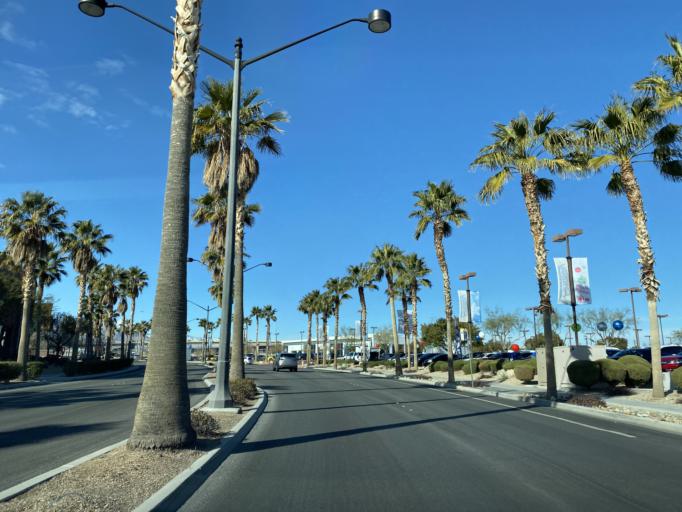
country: US
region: Nevada
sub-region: Clark County
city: Las Vegas
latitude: 36.2745
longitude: -115.2579
